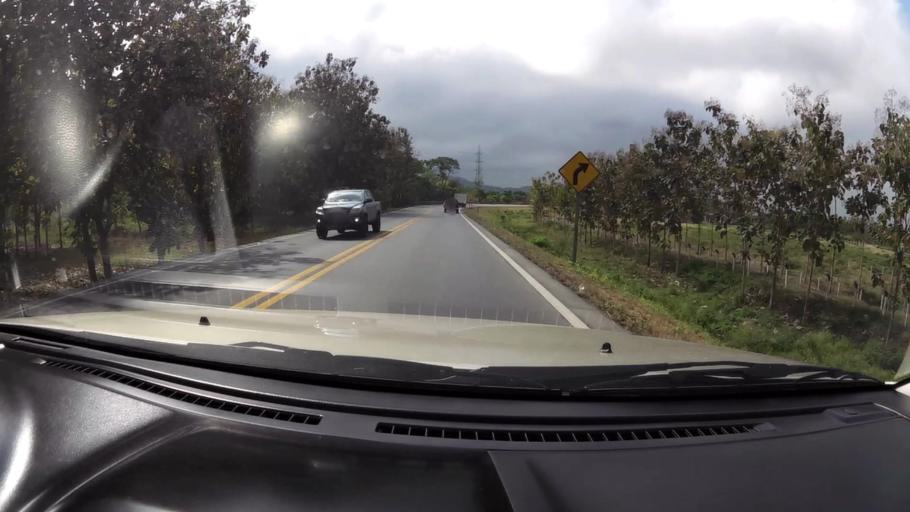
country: EC
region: Guayas
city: Naranjal
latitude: -2.4079
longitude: -79.6243
